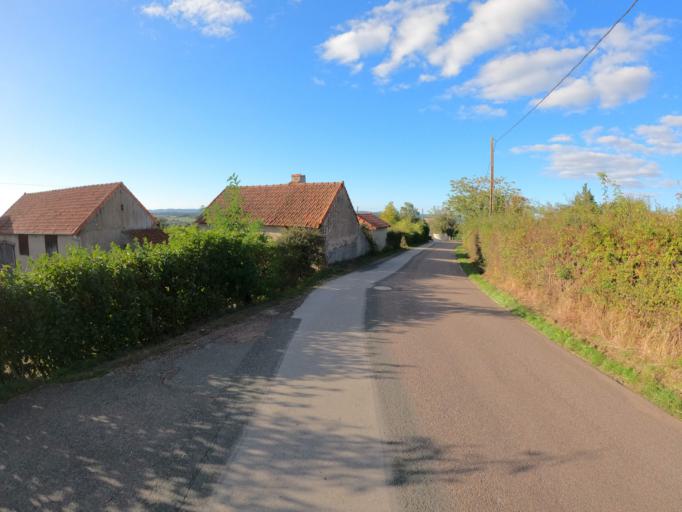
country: FR
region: Bourgogne
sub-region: Departement de Saone-et-Loire
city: Ecuisses
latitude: 46.7489
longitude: 4.5255
